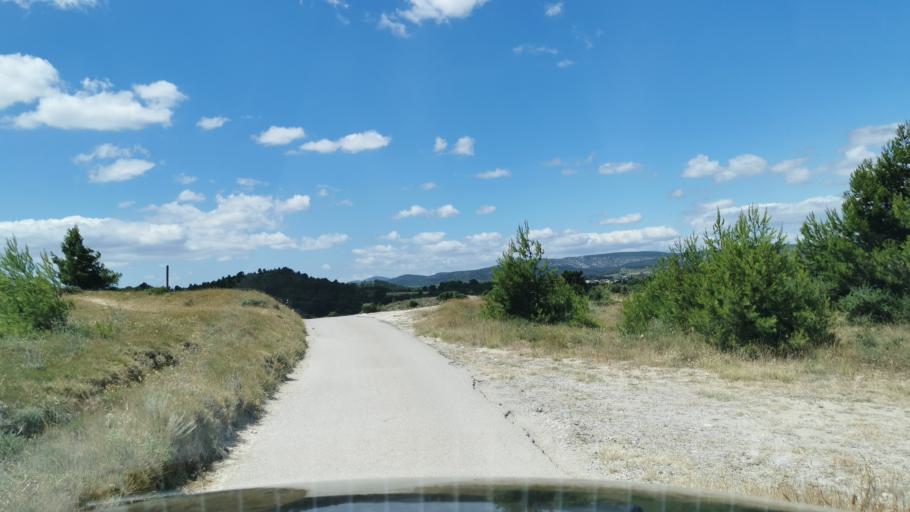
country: FR
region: Languedoc-Roussillon
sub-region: Departement de l'Aude
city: Peyriac-de-Mer
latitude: 43.0896
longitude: 2.9815
